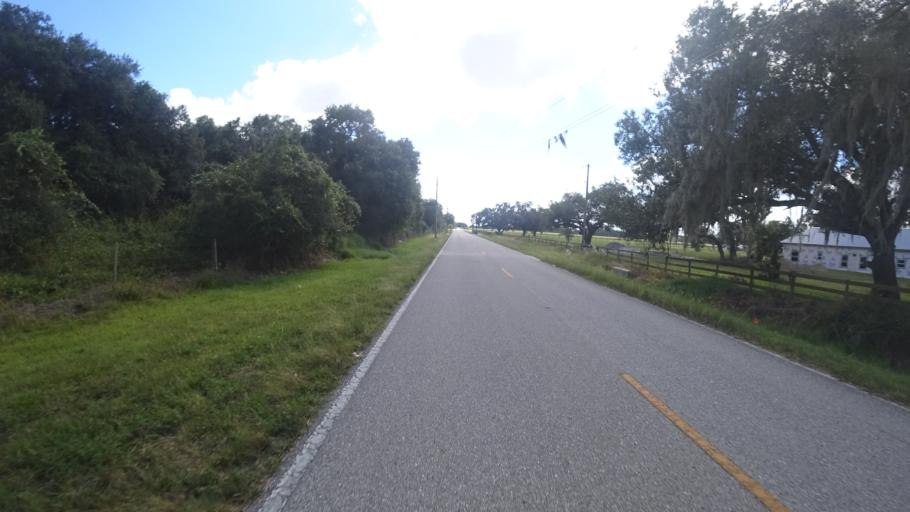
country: US
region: Florida
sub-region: Sarasota County
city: Lake Sarasota
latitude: 27.3417
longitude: -82.1544
